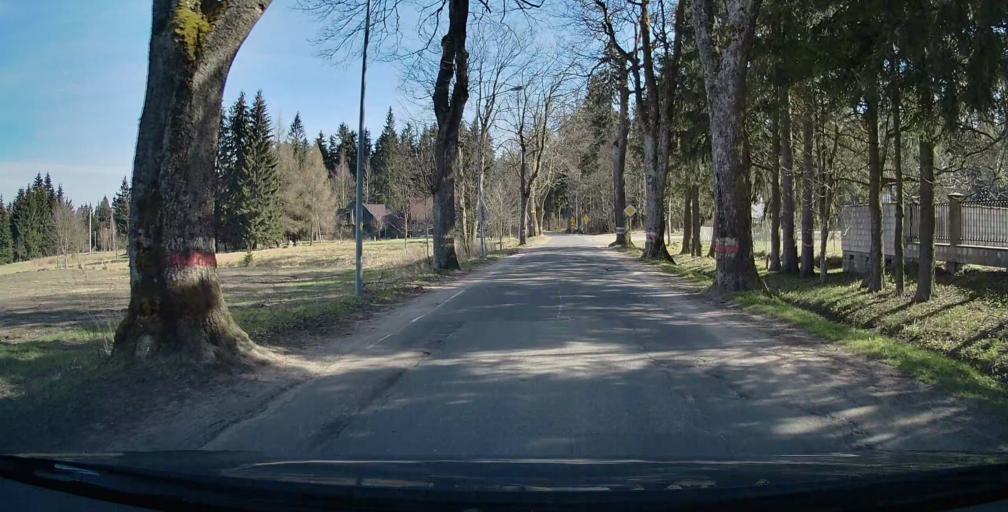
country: CZ
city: Machov
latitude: 50.4743
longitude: 16.3377
